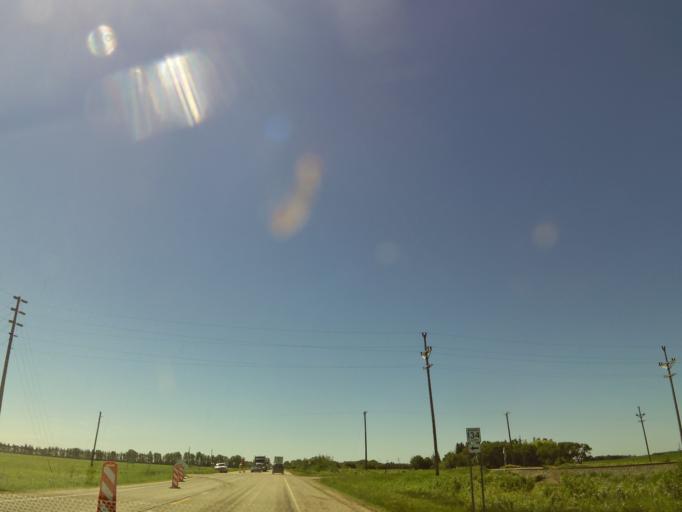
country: US
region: Minnesota
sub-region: Mahnomen County
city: Mahnomen
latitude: 47.4273
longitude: -95.9763
